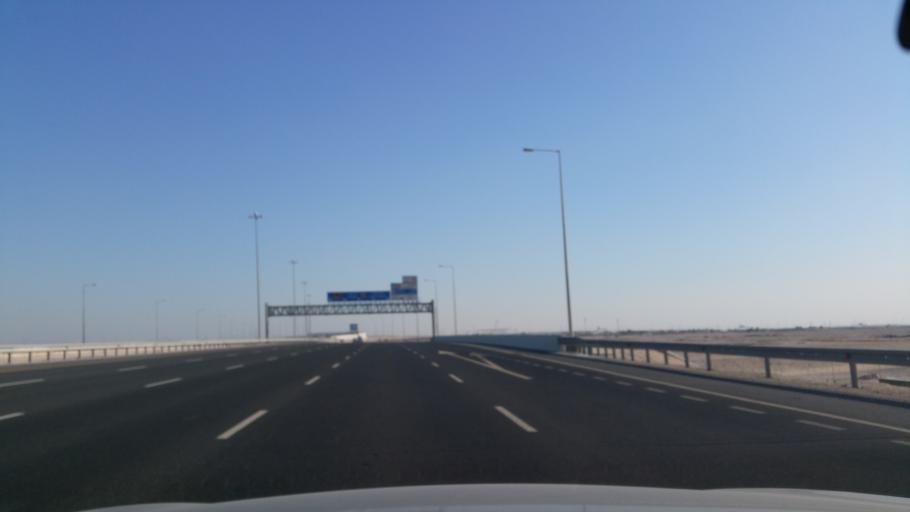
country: QA
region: Al Wakrah
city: Al Wukayr
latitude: 25.1366
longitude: 51.4773
